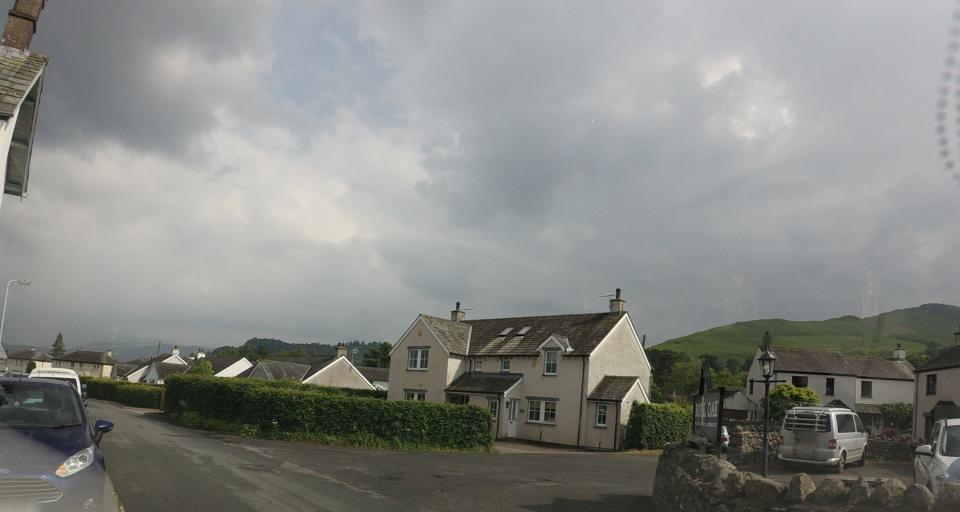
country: GB
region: England
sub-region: Cumbria
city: Keswick
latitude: 54.6024
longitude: -3.1908
